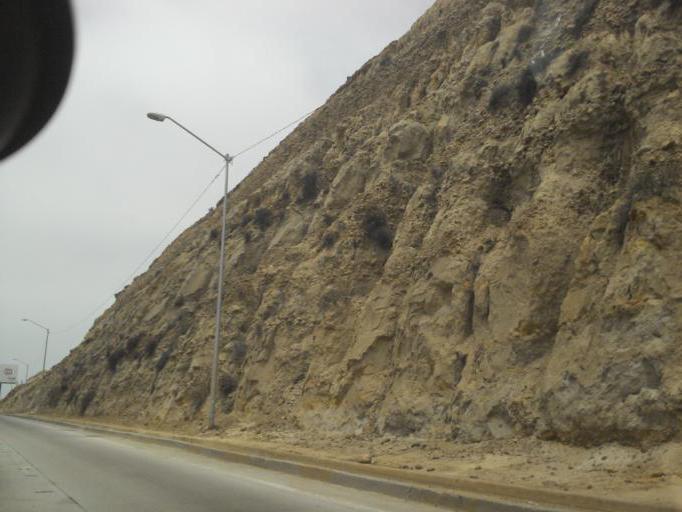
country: US
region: California
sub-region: San Diego County
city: Imperial Beach
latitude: 32.5353
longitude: -117.1036
